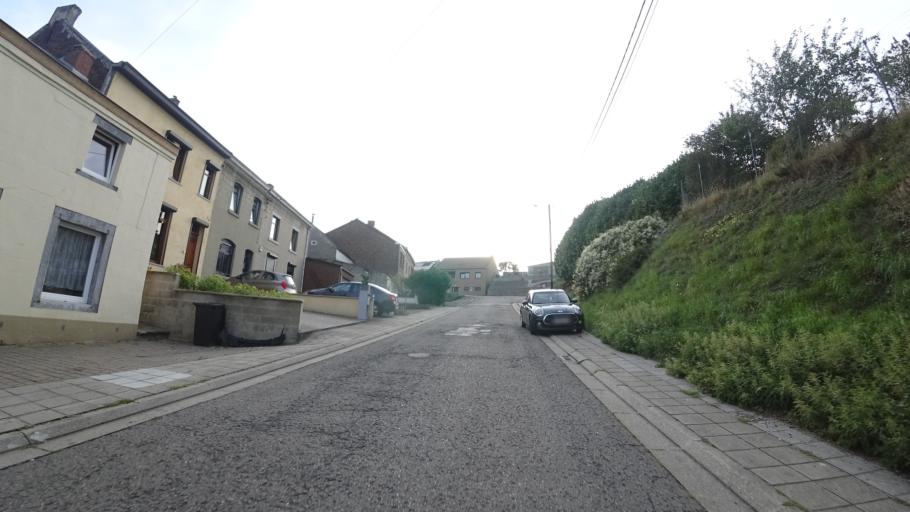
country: BE
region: Wallonia
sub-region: Province de Namur
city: Fosses-la-Ville
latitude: 50.4420
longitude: 4.6743
